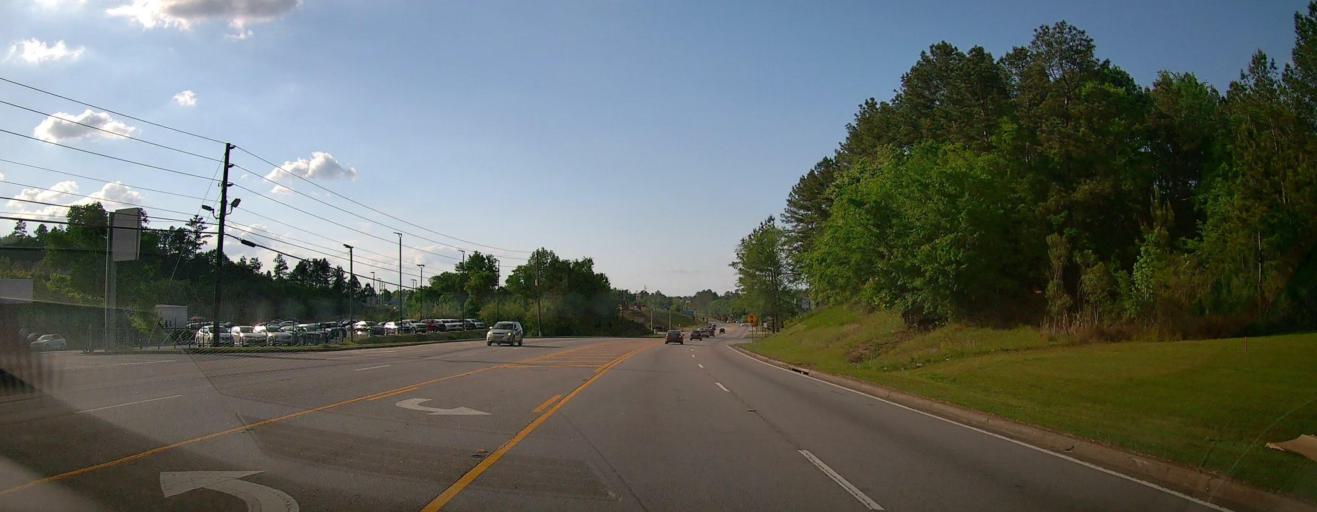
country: US
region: Georgia
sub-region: Baldwin County
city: Milledgeville
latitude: 33.1145
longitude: -83.2598
